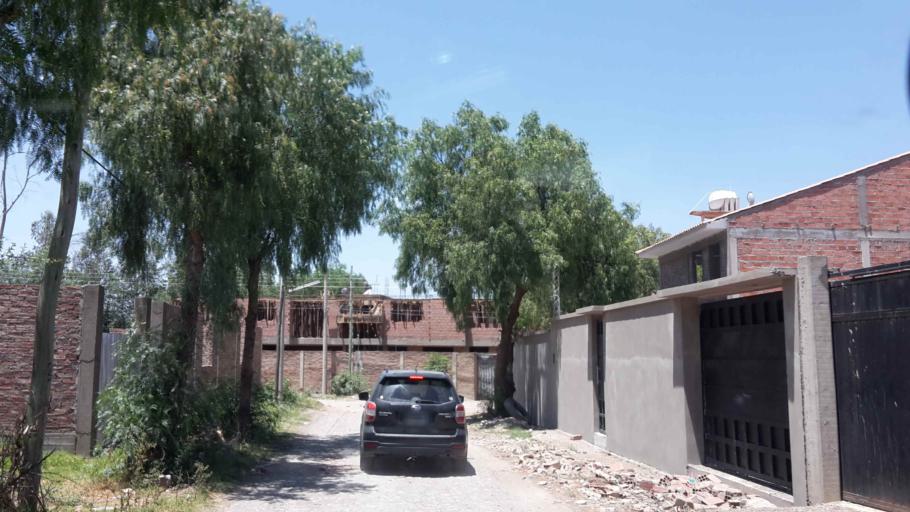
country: BO
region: Cochabamba
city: Cochabamba
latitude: -17.3708
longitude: -66.1961
